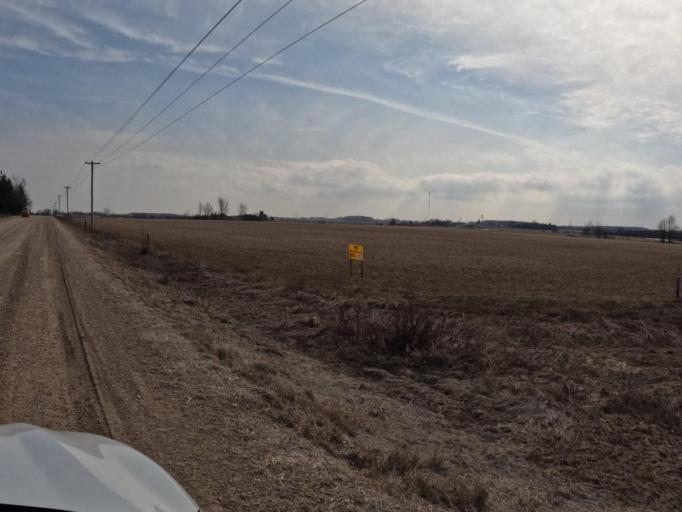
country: CA
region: Ontario
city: Orangeville
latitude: 43.8831
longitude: -80.2975
